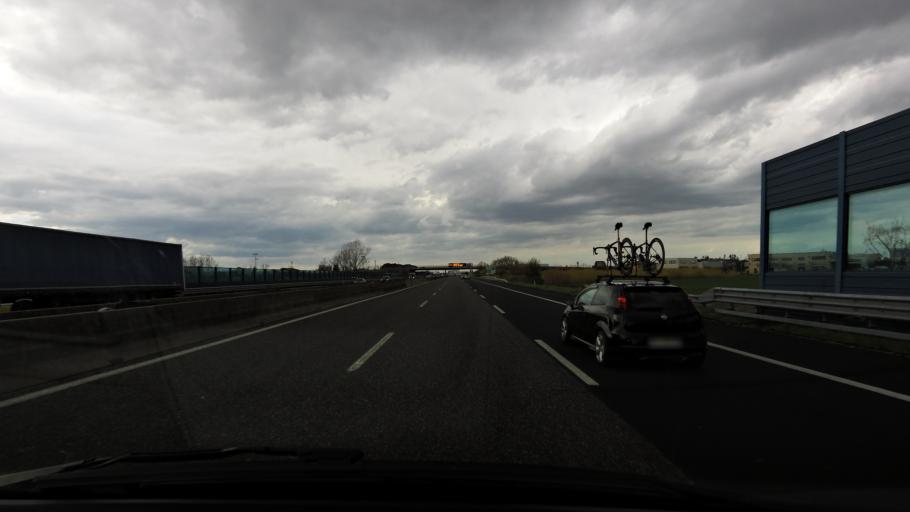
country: IT
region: Emilia-Romagna
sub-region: Forli-Cesena
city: San Mauro Pascoli
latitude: 44.1107
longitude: 12.4221
